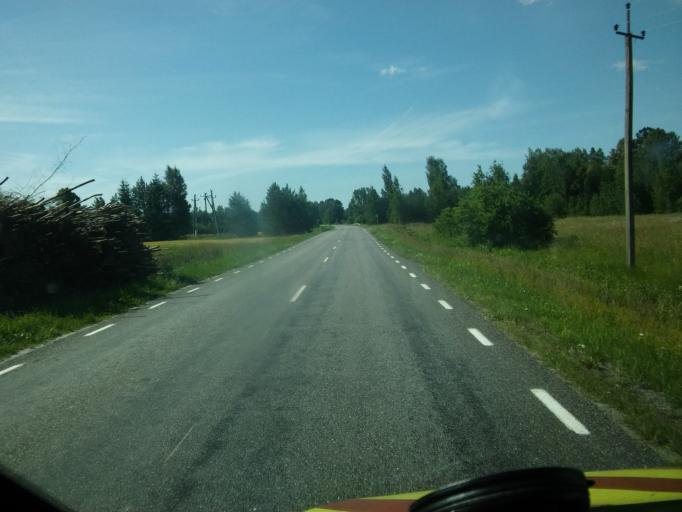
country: EE
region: Paernumaa
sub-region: Paikuse vald
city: Paikuse
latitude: 58.3233
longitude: 24.6865
